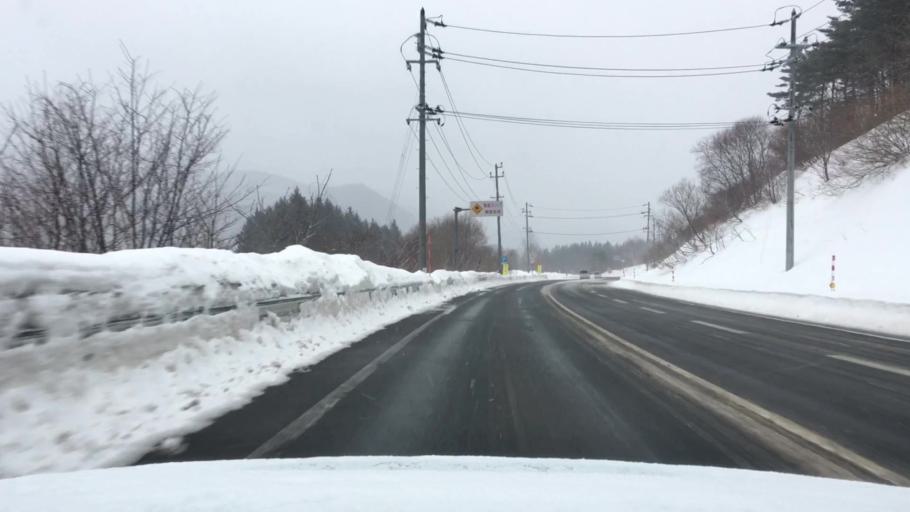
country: JP
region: Akita
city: Hanawa
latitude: 40.0288
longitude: 140.9856
